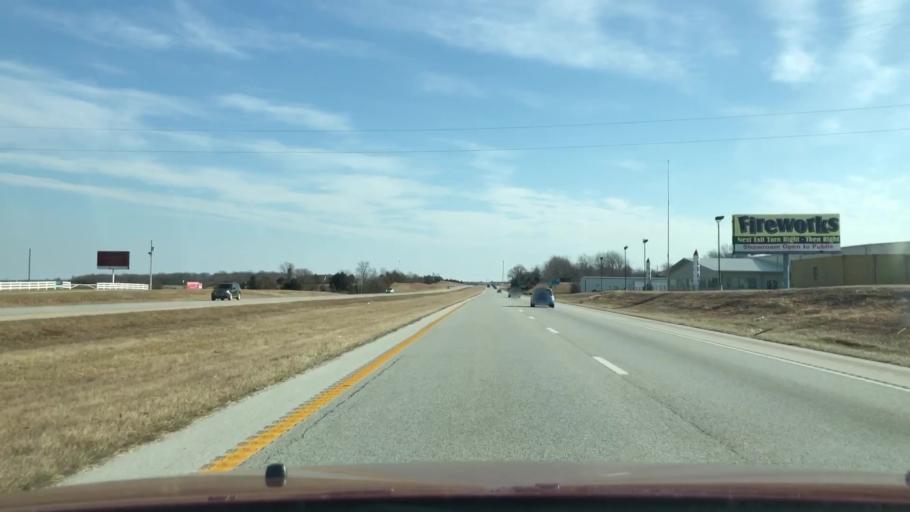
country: US
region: Missouri
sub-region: Webster County
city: Seymour
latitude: 37.1564
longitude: -92.7817
